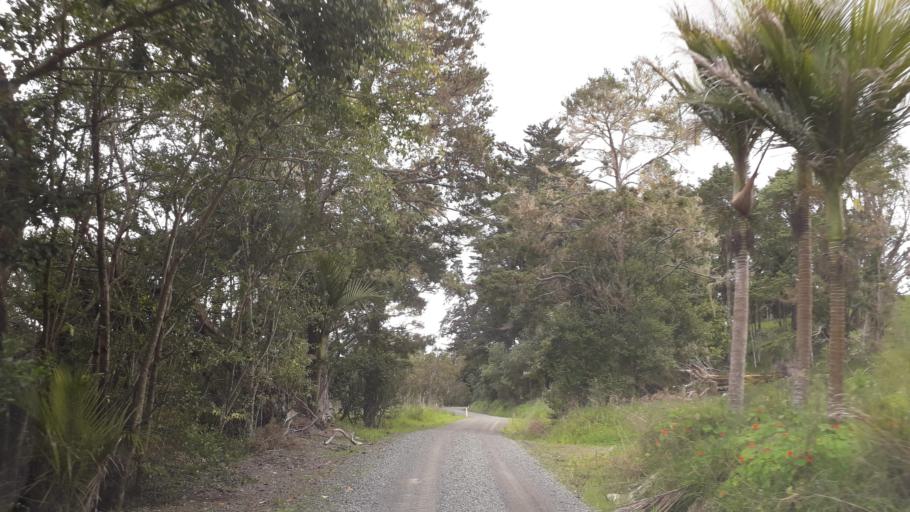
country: NZ
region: Northland
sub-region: Far North District
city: Waimate North
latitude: -35.3167
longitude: 173.5695
